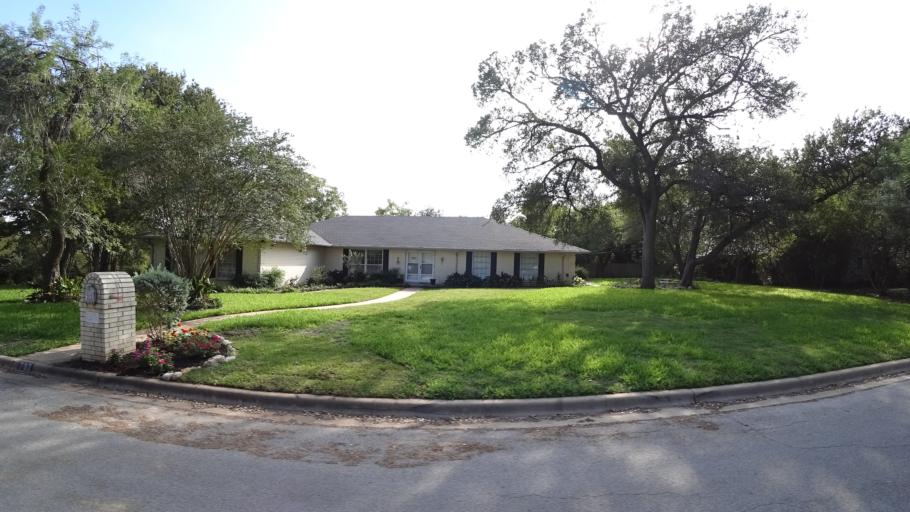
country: US
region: Texas
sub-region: Travis County
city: Rollingwood
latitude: 30.2779
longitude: -97.8003
